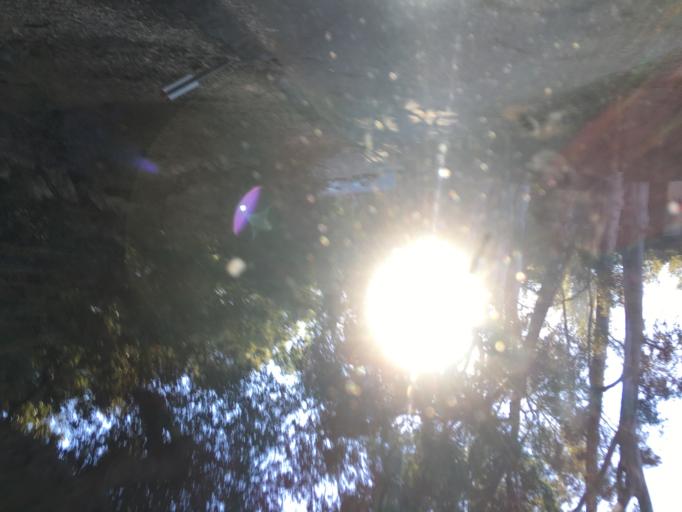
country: US
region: California
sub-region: Los Angeles County
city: Westlake Village
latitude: 34.0899
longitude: -118.8174
